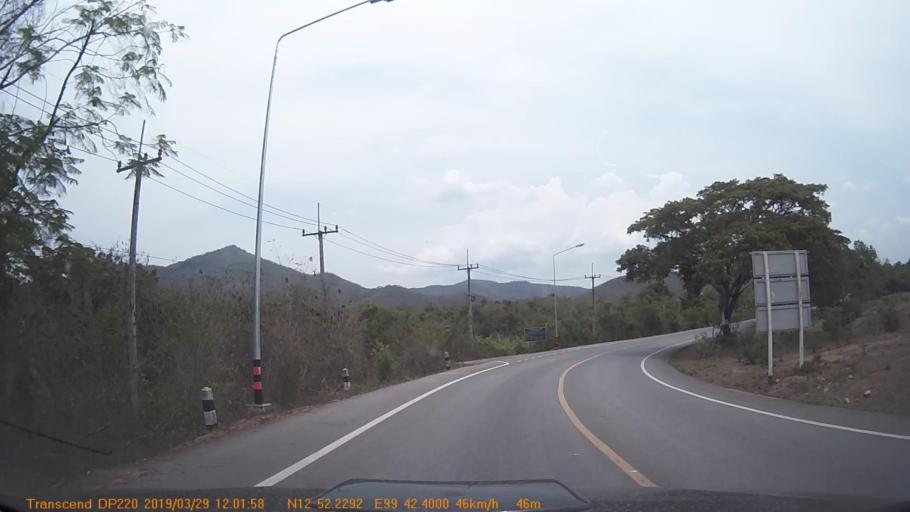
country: TH
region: Phetchaburi
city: Kaeng Krachan
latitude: 12.8705
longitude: 99.7070
